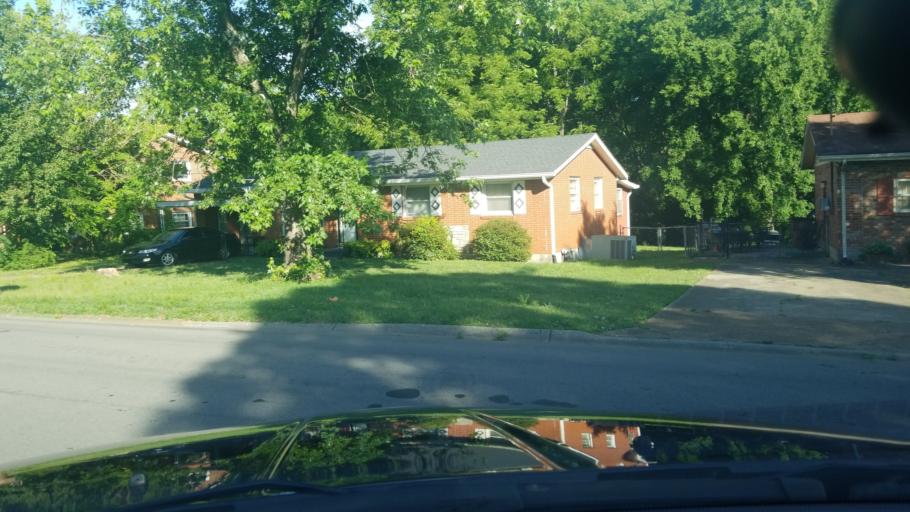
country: US
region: Tennessee
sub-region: Davidson County
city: Nashville
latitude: 36.2381
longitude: -86.7692
